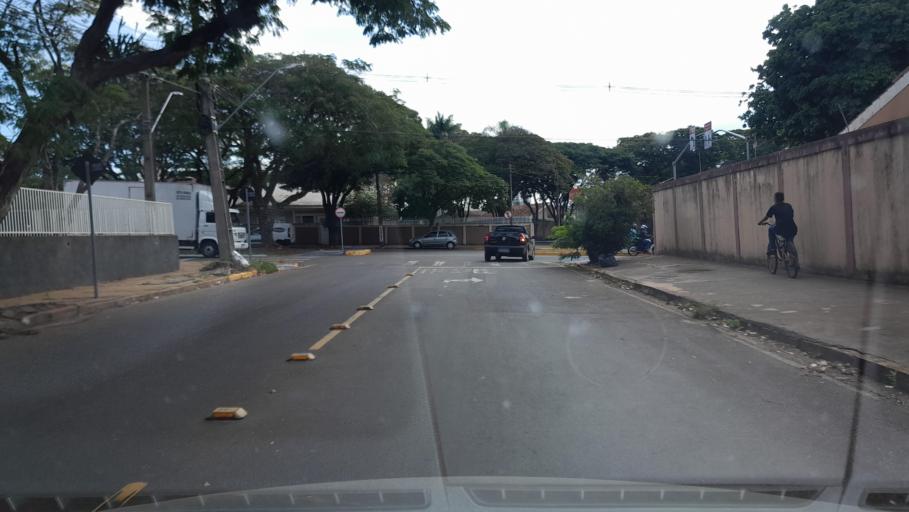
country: BR
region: Parana
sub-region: Umuarama
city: Umuarama
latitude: -23.7694
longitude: -53.3108
